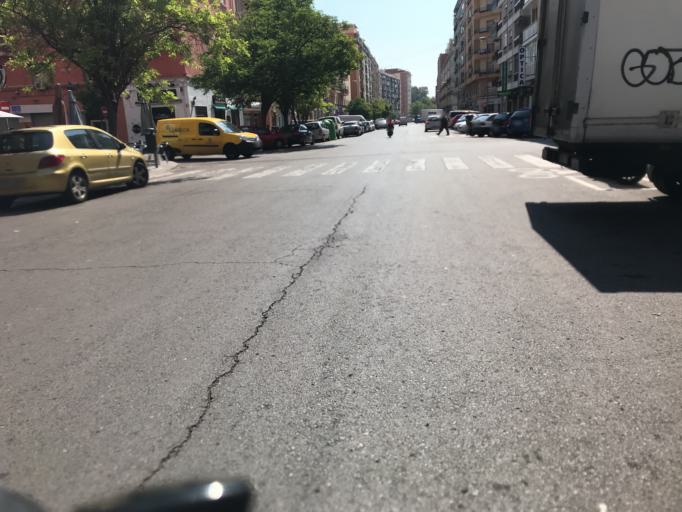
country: ES
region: Valencia
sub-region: Provincia de Valencia
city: Valencia
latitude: 39.4678
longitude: -0.3498
